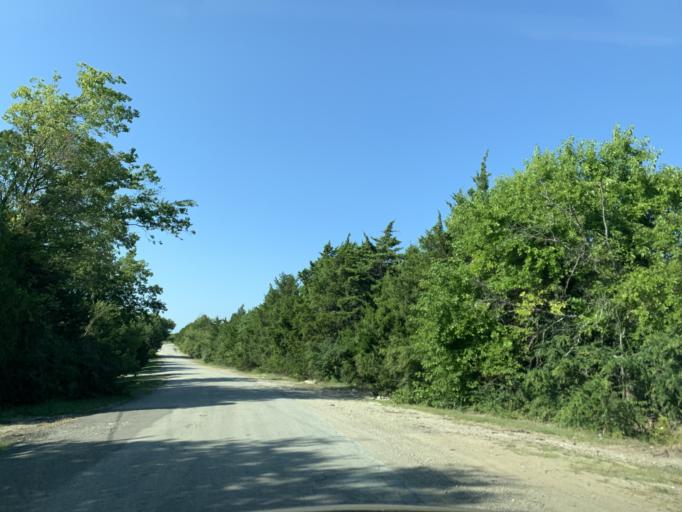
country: US
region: Texas
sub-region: Dallas County
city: Hutchins
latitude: 32.6613
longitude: -96.7465
